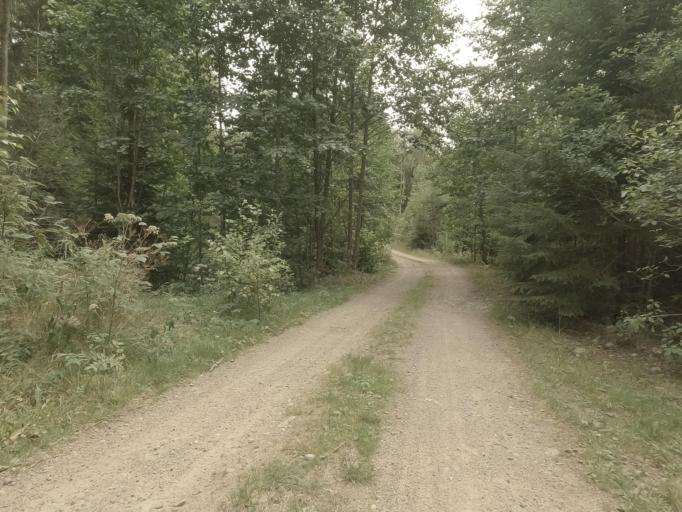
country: RU
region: Leningrad
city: Kamennogorsk
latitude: 61.0077
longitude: 29.1869
